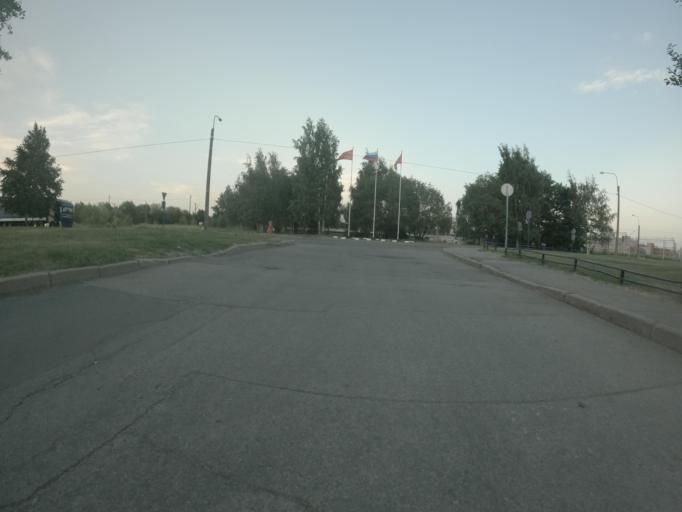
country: RU
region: St.-Petersburg
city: Krasnogvargeisky
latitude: 59.9373
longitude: 30.4452
